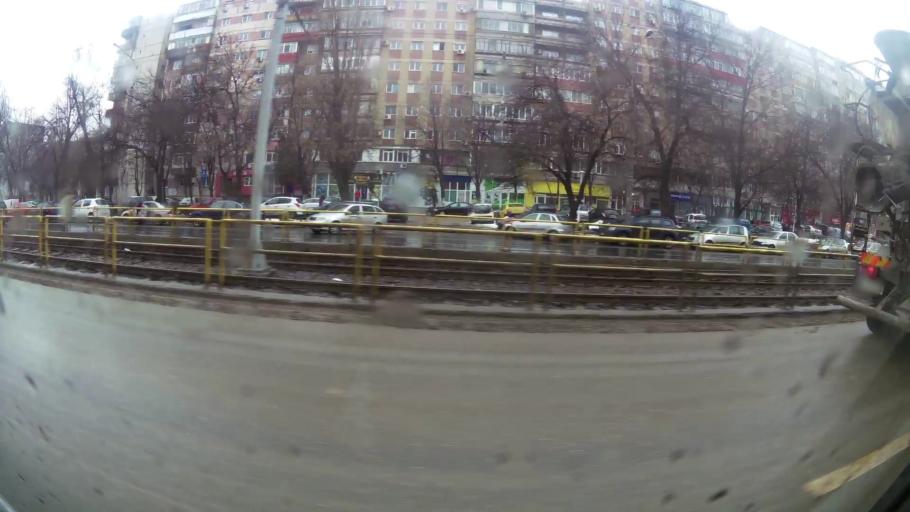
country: RO
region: Ilfov
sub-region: Comuna Chiajna
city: Rosu
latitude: 44.4168
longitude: 26.0344
